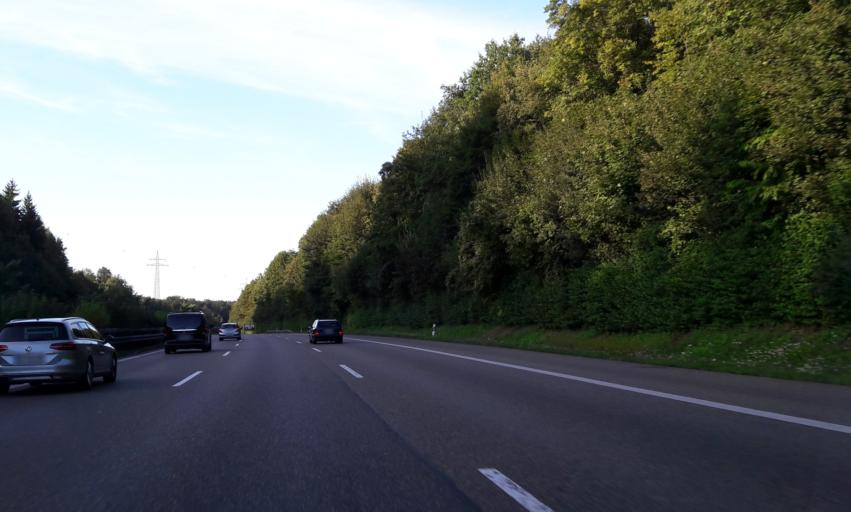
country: DE
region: Baden-Wuerttemberg
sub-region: Regierungsbezirk Stuttgart
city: Ilsfeld
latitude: 49.0284
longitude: 9.2533
